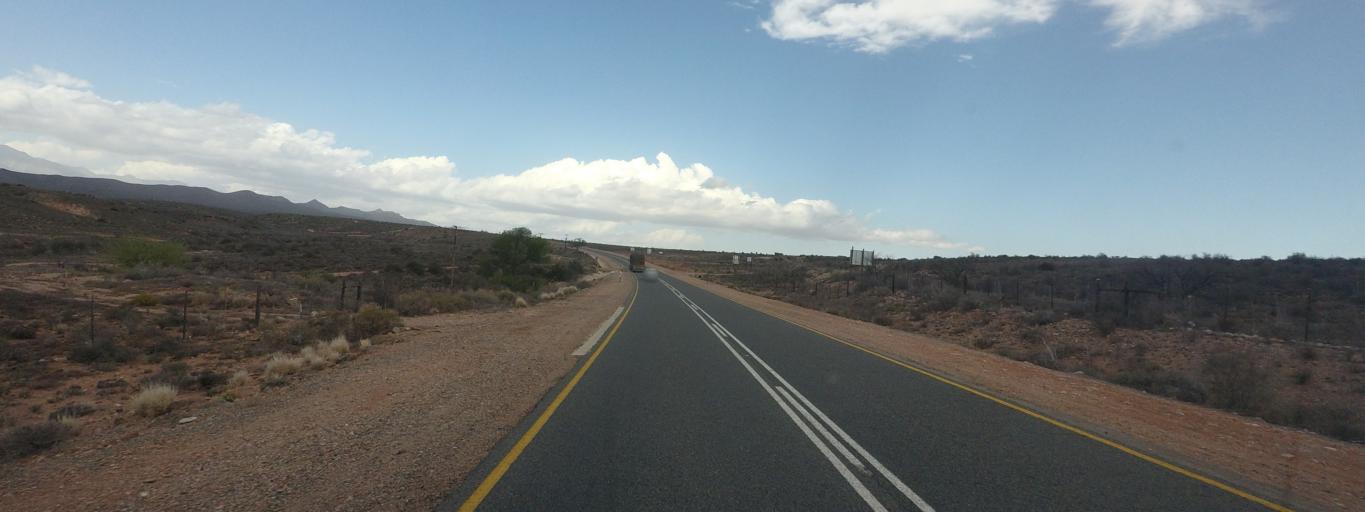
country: ZA
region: Western Cape
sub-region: Eden District Municipality
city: Ladismith
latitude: -33.5328
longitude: 21.7060
